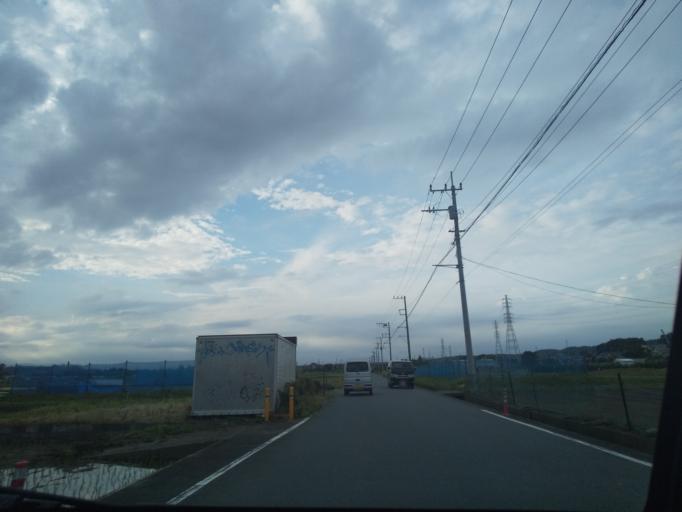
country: JP
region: Kanagawa
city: Zama
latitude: 35.4907
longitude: 139.3850
